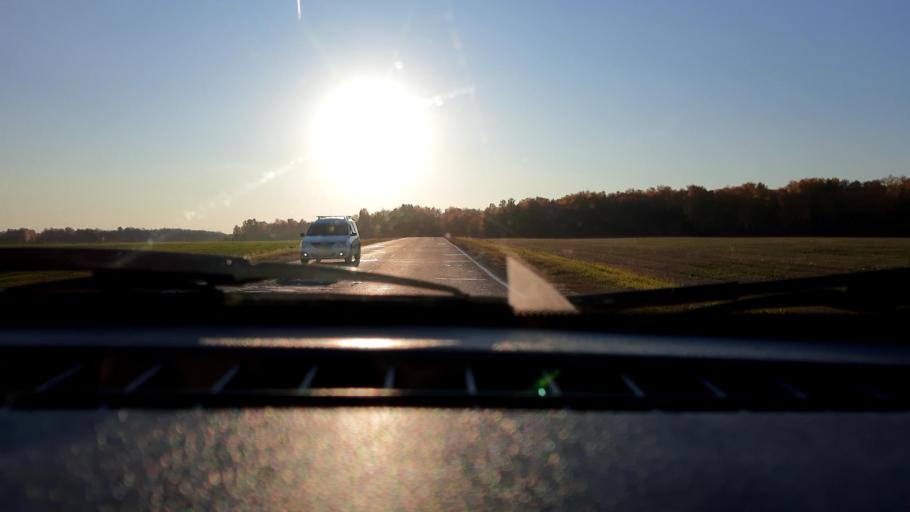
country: RU
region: Bashkortostan
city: Mikhaylovka
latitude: 54.8203
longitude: 55.7447
